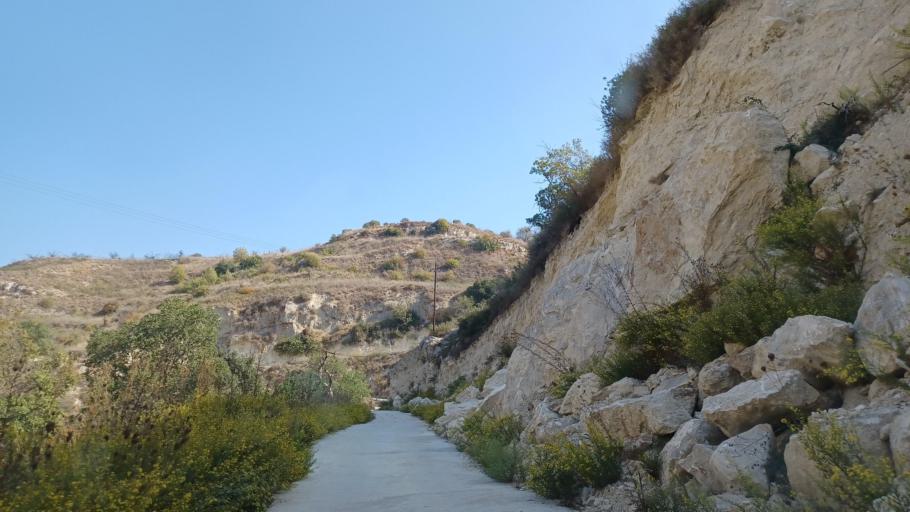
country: CY
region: Pafos
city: Tala
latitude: 34.9090
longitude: 32.4580
